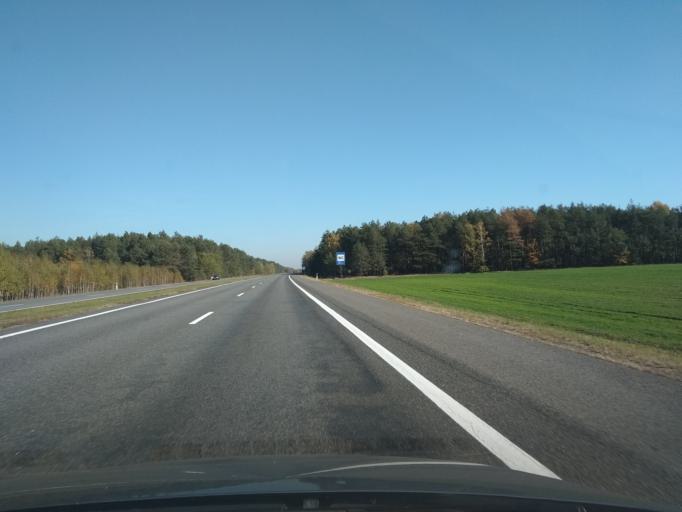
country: BY
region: Brest
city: Antopal'
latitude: 52.3355
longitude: 24.6408
